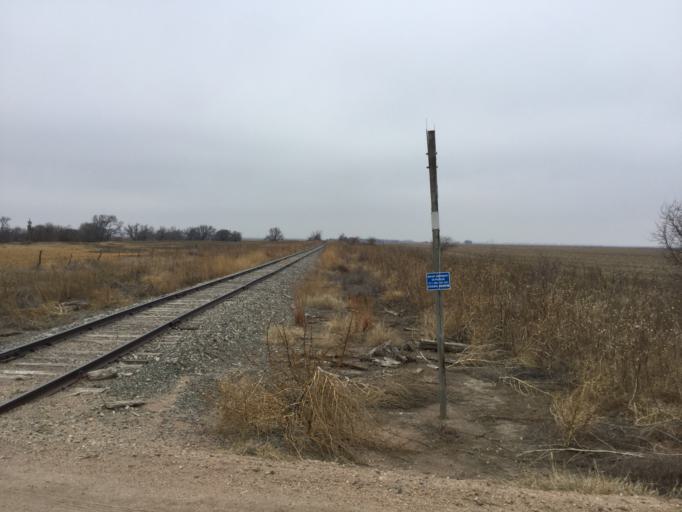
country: US
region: Kansas
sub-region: Edwards County
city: Kinsley
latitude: 38.1965
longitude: -99.4602
